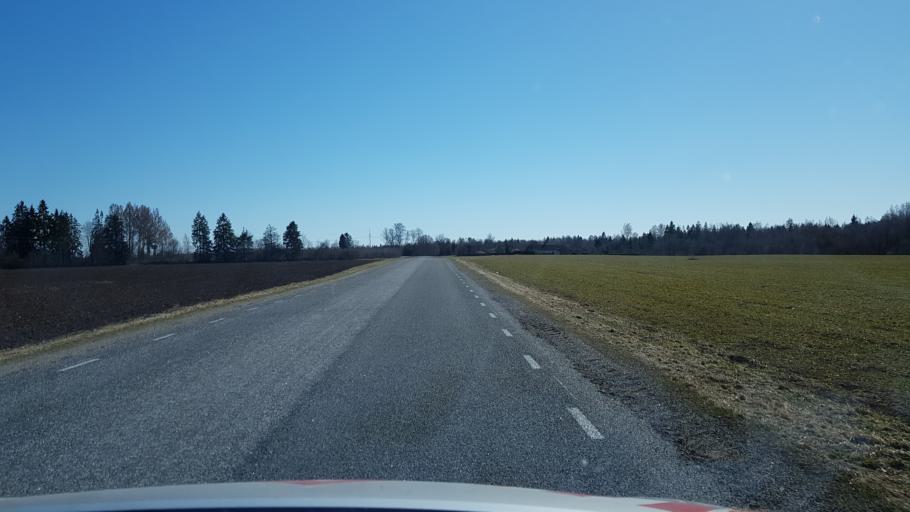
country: EE
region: Laeaene-Virumaa
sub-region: Someru vald
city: Someru
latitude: 59.3821
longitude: 26.4413
